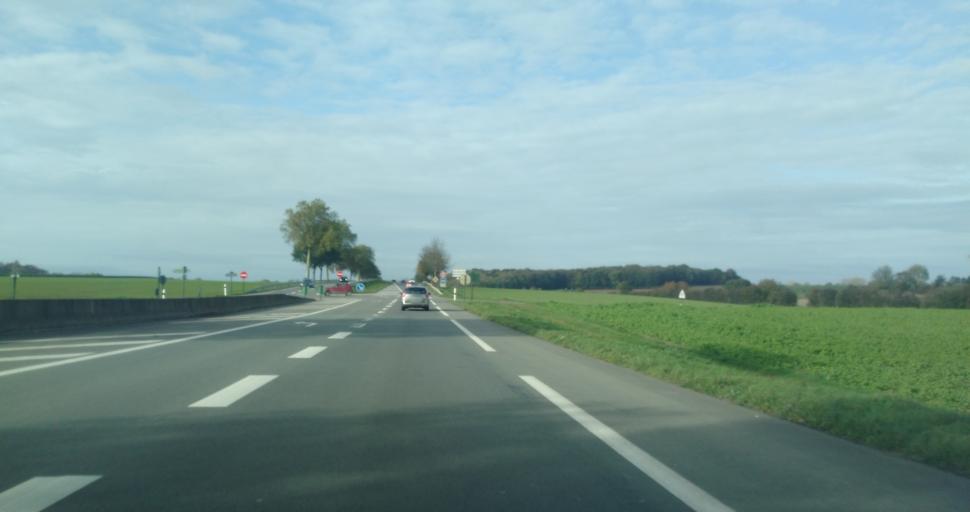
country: FR
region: Nord-Pas-de-Calais
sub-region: Departement du Pas-de-Calais
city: Saint-Pol-sur-Ternoise
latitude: 50.3627
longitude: 2.4452
